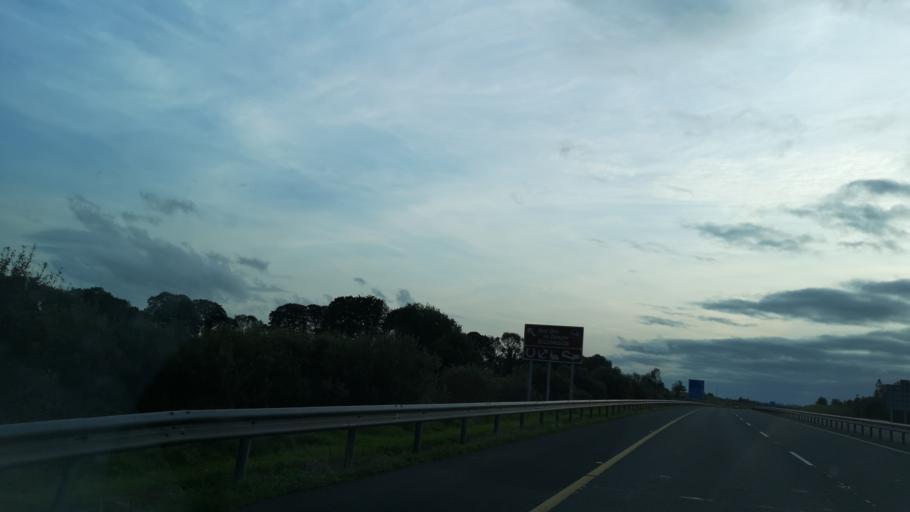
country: IE
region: Connaught
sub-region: County Galway
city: Ballinasloe
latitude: 53.3194
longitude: -8.1587
